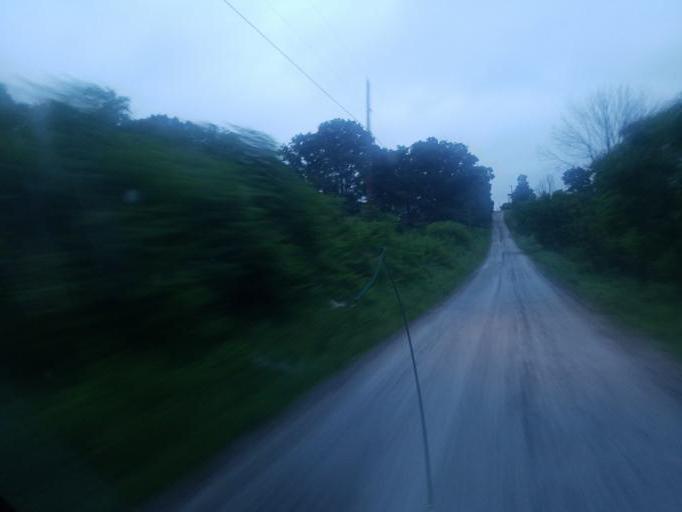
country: US
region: Ohio
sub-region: Carroll County
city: Carrollton
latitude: 40.5014
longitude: -81.0362
